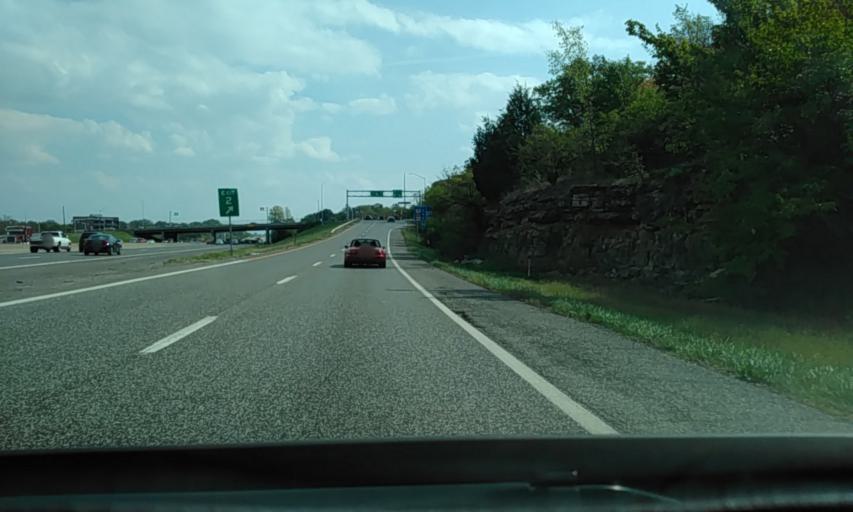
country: US
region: Missouri
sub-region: Saint Louis County
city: Concord
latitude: 38.5138
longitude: -90.3750
